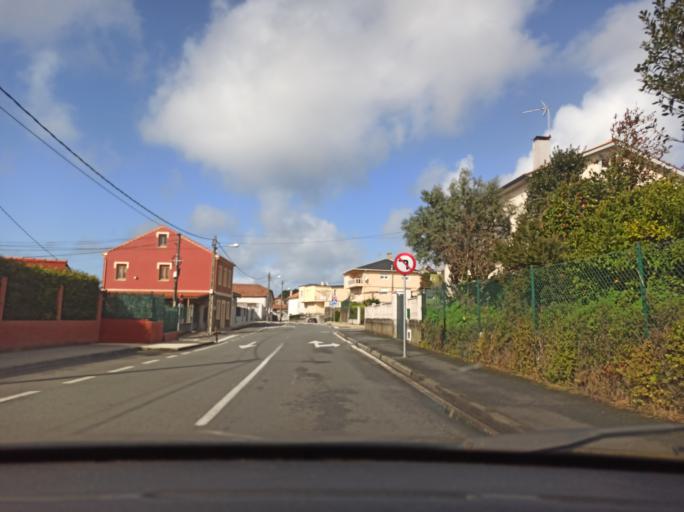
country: ES
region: Galicia
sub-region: Provincia da Coruna
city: Cambre
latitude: 43.3282
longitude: -8.3539
